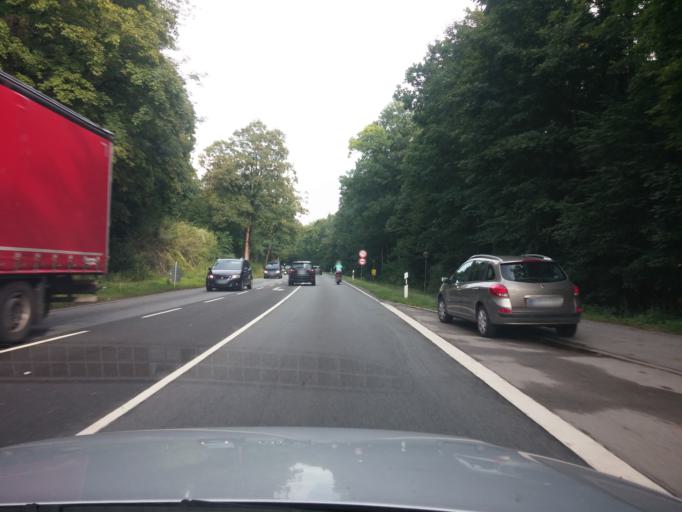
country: DE
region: Bavaria
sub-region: Upper Bavaria
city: Vaterstetten
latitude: 48.0919
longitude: 11.7835
